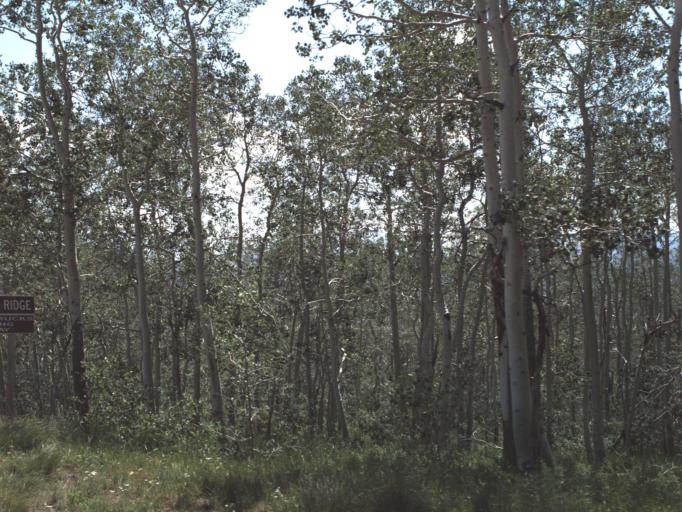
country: US
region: Utah
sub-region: Weber County
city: Wolf Creek
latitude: 41.4221
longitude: -111.5217
